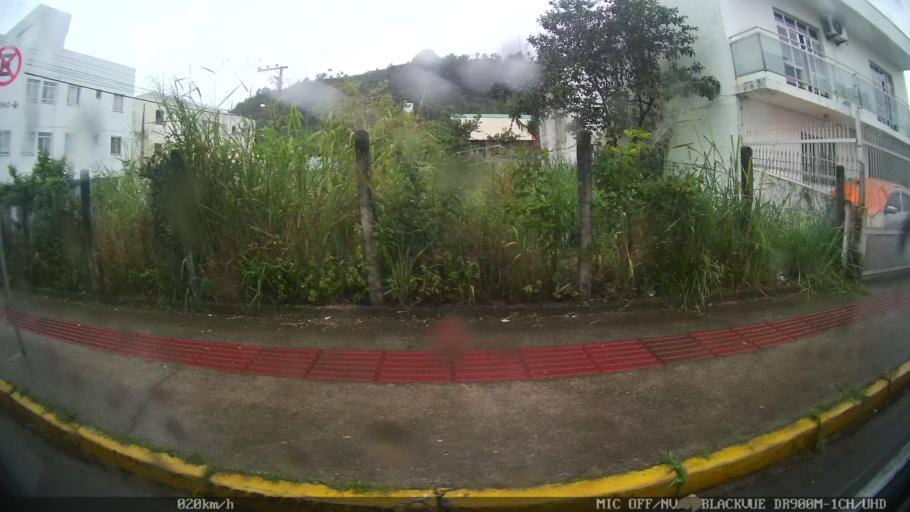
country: BR
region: Santa Catarina
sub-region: Itajai
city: Itajai
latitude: -26.9154
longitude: -48.6662
